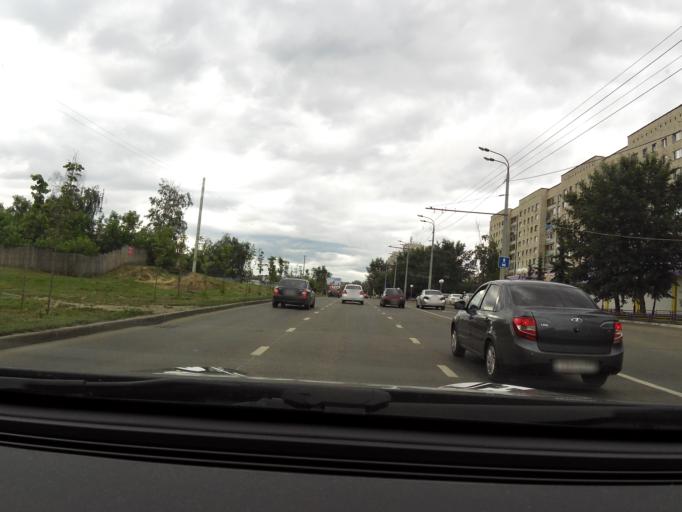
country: RU
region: Tatarstan
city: Staroye Arakchino
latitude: 55.8225
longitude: 49.0487
